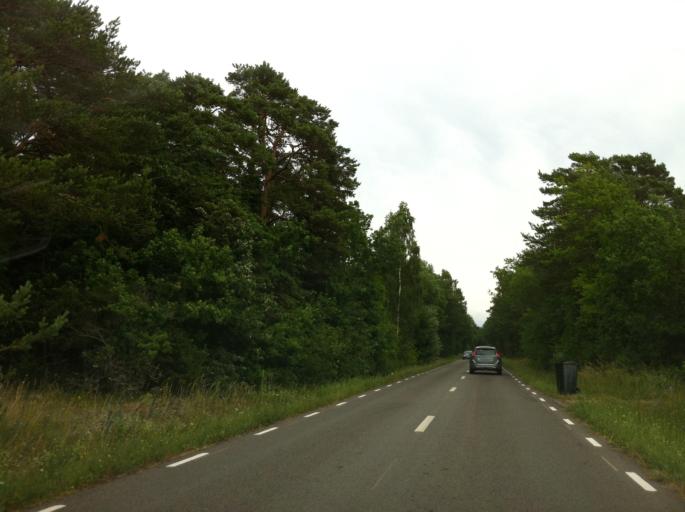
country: SE
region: Kalmar
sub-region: Vasterviks Kommun
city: Vaestervik
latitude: 57.3493
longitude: 17.0349
